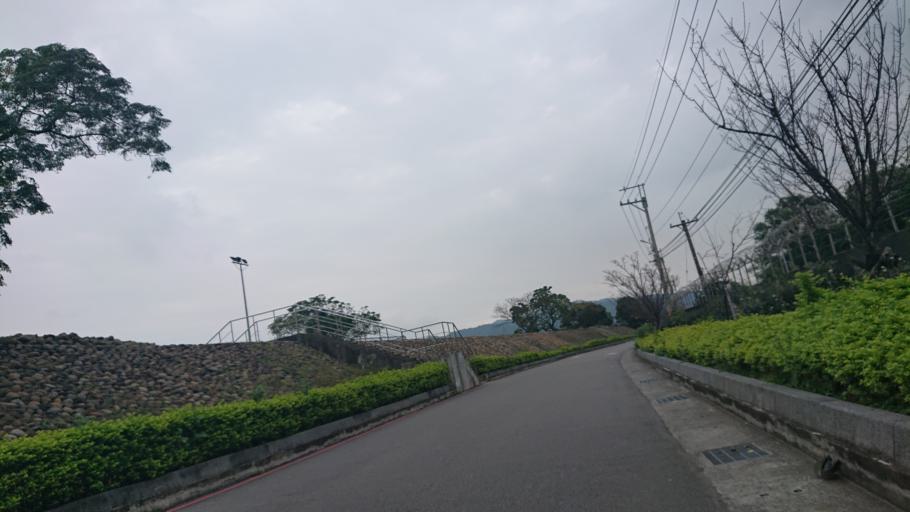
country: TW
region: Taiwan
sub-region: Taoyuan
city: Taoyuan
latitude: 24.9368
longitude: 121.3516
